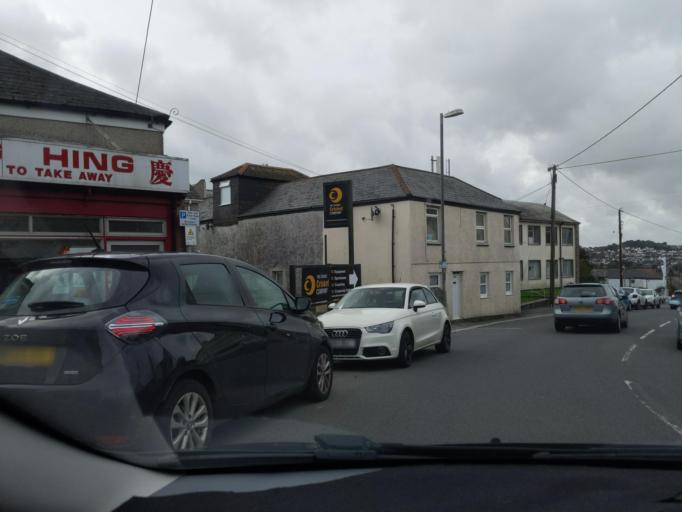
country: GB
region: England
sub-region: Cornwall
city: St Austell
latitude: 50.3378
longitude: -4.7872
